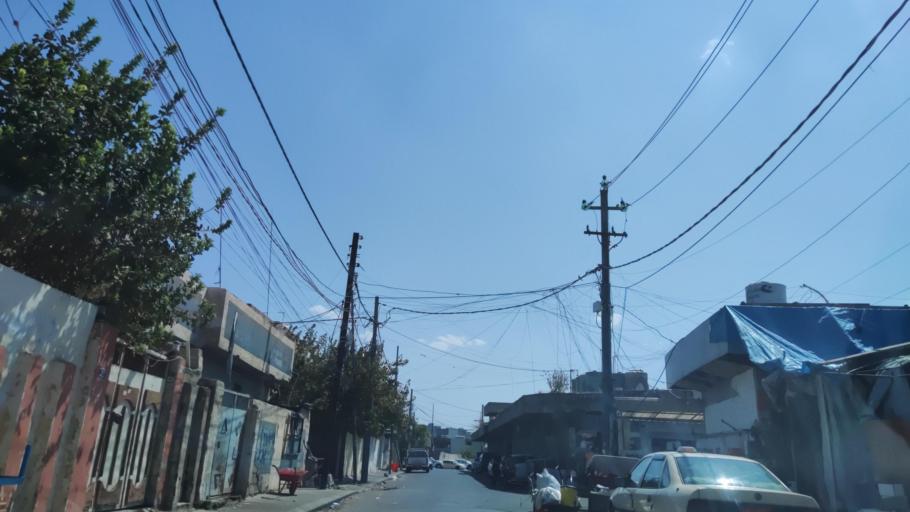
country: IQ
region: Arbil
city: Erbil
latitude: 36.1873
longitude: 44.0211
